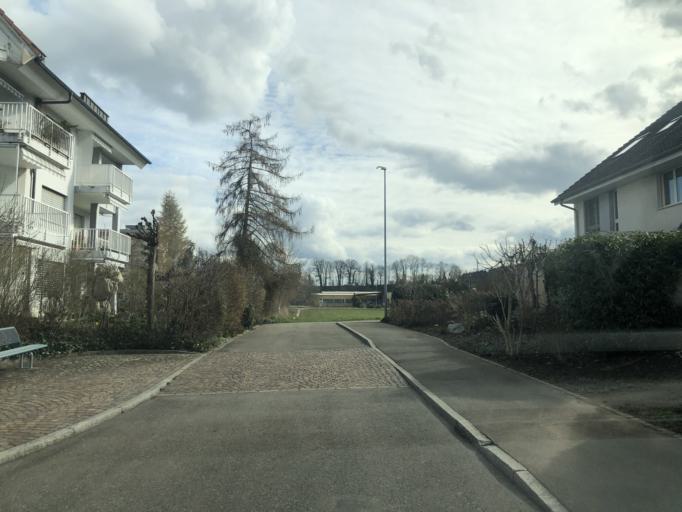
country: CH
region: Aargau
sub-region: Bezirk Baden
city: Mellingen
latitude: 47.4111
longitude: 8.2696
